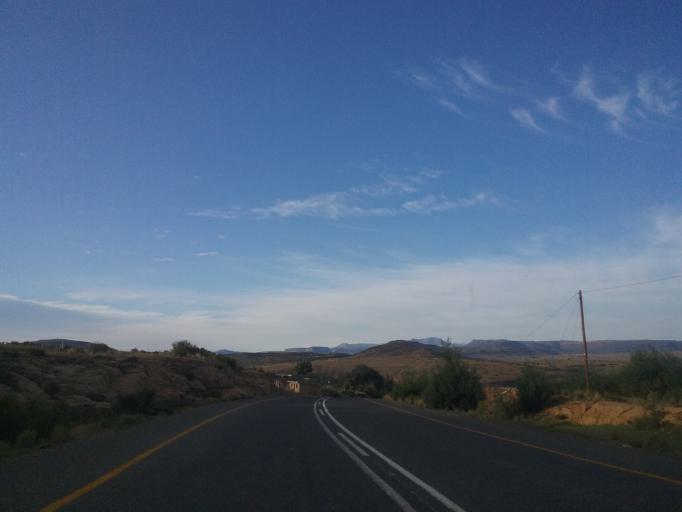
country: LS
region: Mohale's Hoek District
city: Mohale's Hoek
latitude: -30.2694
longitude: 27.4555
